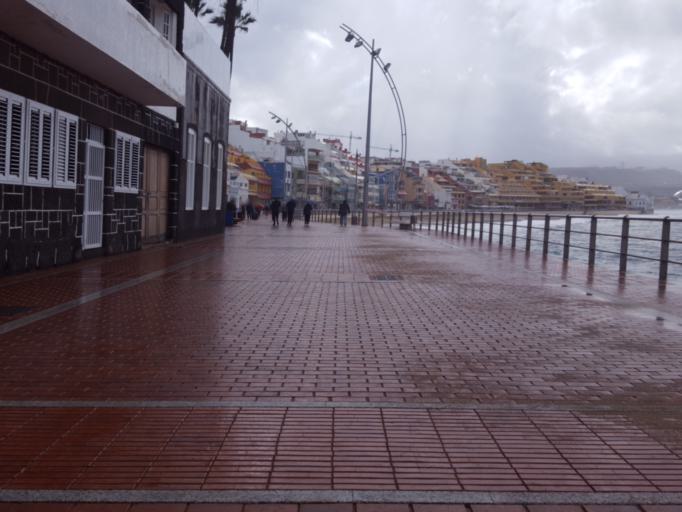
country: ES
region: Canary Islands
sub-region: Provincia de Las Palmas
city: Las Palmas de Gran Canaria
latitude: 28.1391
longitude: -15.4366
